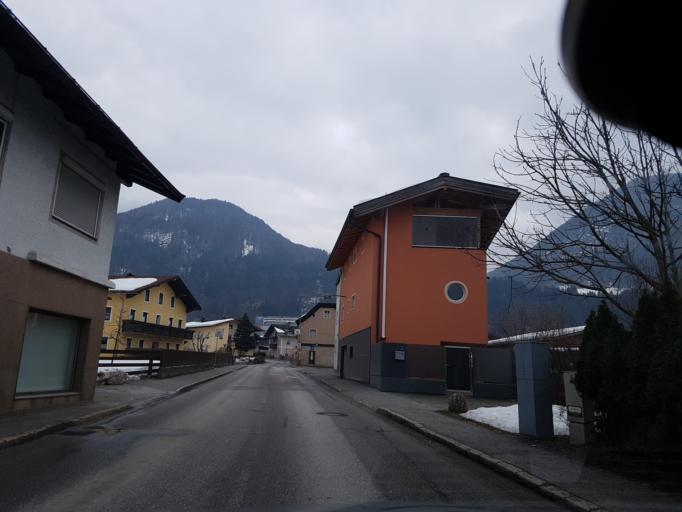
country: AT
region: Tyrol
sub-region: Politischer Bezirk Kufstein
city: Worgl
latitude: 47.4842
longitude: 12.0649
